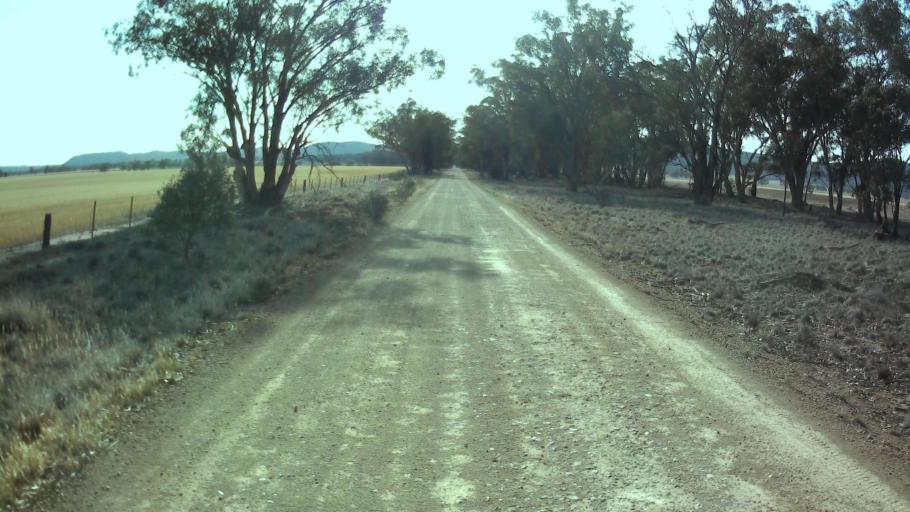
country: AU
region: New South Wales
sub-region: Weddin
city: Grenfell
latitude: -33.7966
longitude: 148.0828
